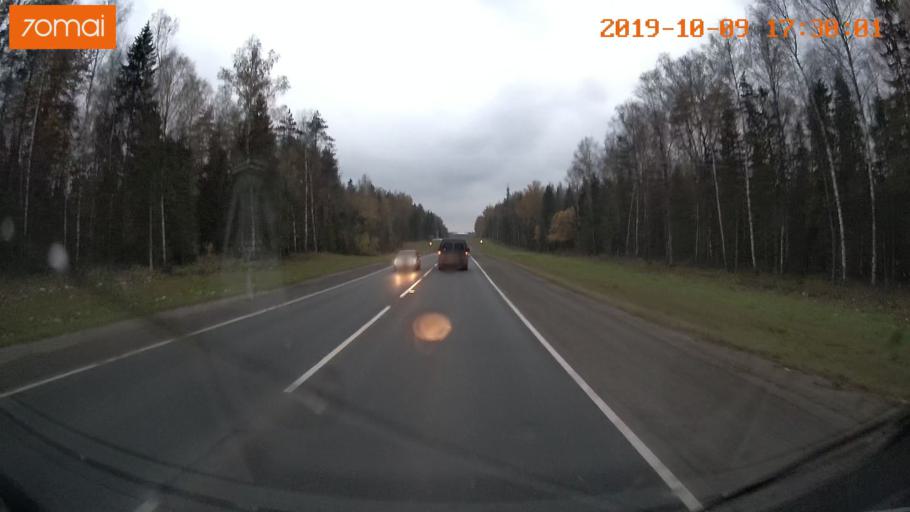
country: RU
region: Ivanovo
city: Bogorodskoye
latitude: 57.1458
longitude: 41.0536
